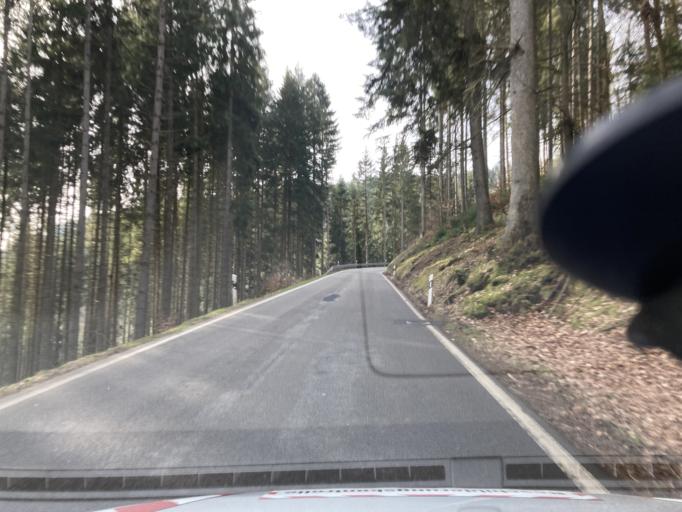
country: DE
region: Baden-Wuerttemberg
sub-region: Karlsruhe Region
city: Neuweiler
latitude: 48.6823
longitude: 8.6414
